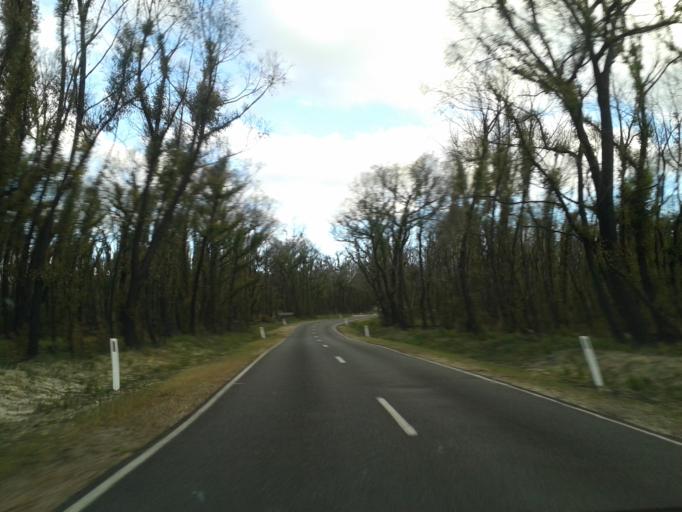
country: AU
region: Victoria
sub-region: Northern Grampians
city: Stawell
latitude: -37.1236
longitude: 142.4213
